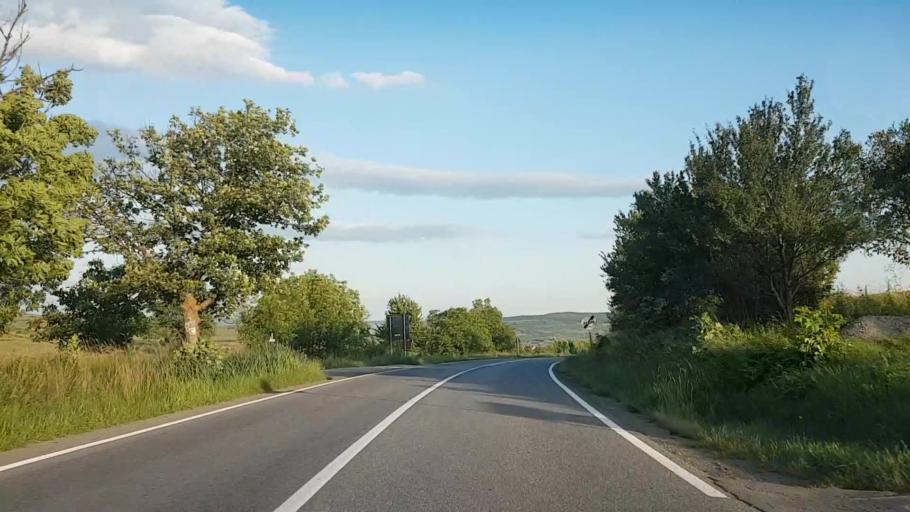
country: RO
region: Harghita
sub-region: Comuna Lupeni
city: Lupeni
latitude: 46.3940
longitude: 25.2136
